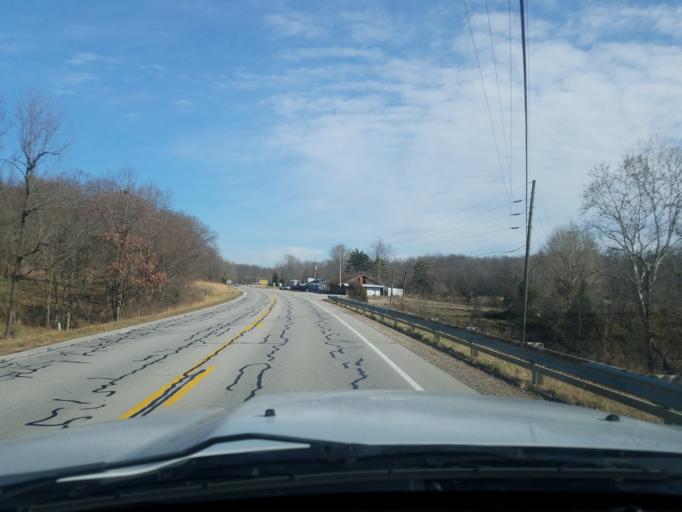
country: US
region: Indiana
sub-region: Crawford County
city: English
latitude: 38.3323
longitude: -86.5724
